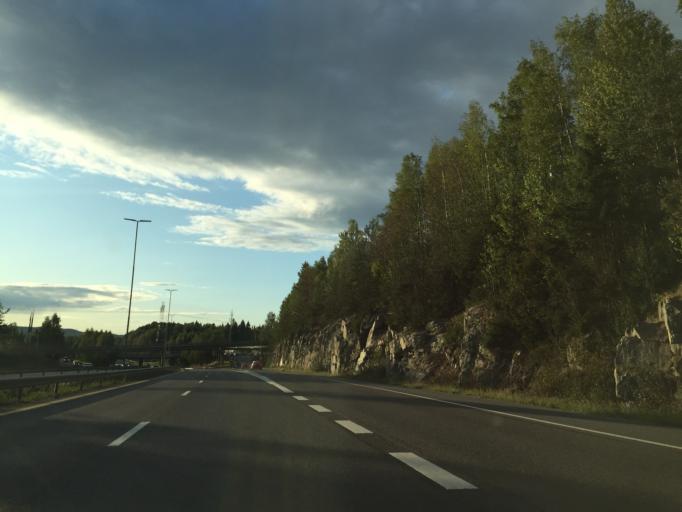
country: NO
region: Akershus
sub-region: Lorenskog
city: Kjenn
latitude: 59.9345
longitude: 10.9403
